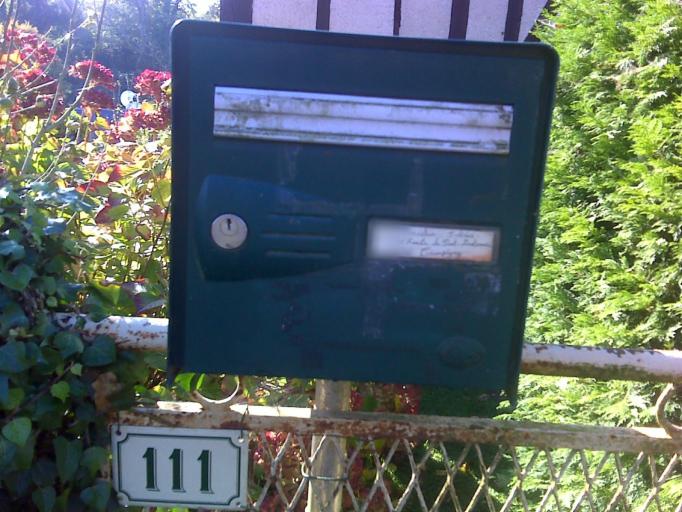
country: FR
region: Haute-Normandie
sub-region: Departement de l'Eure
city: Manneville-sur-Risle
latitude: 49.3102
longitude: 0.5518
